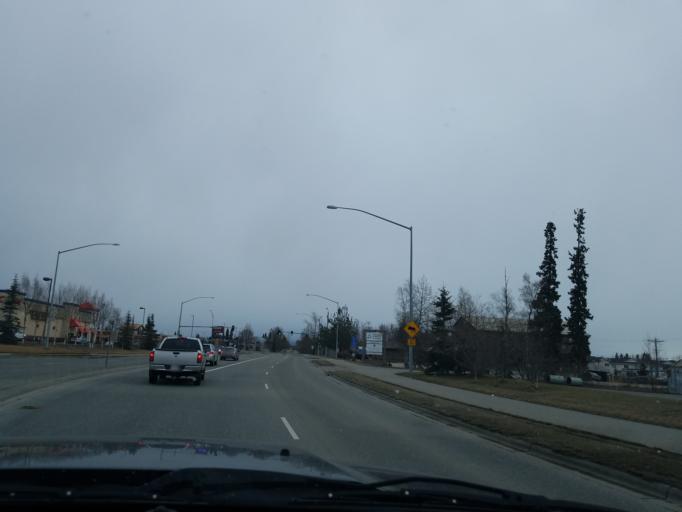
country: US
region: Alaska
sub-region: Anchorage Municipality
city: Anchorage
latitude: 61.1423
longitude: -149.8478
